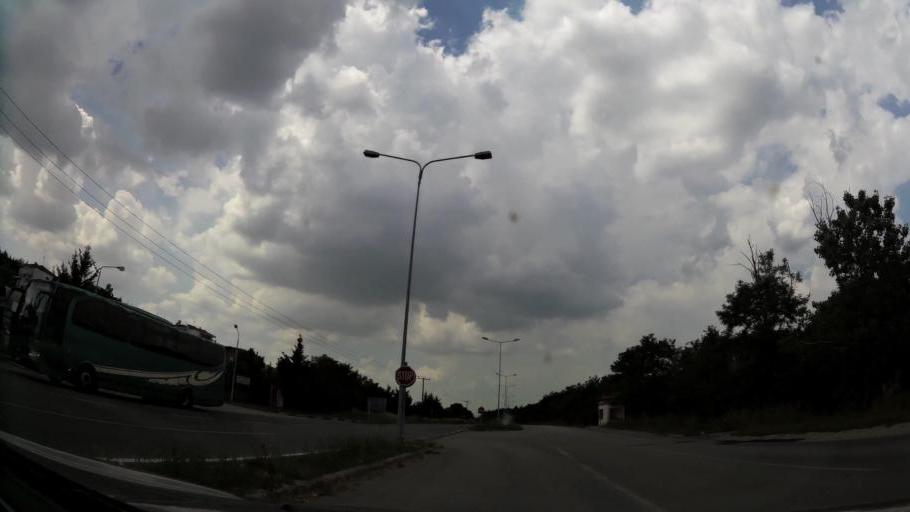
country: GR
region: West Macedonia
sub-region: Nomos Kozanis
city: Koila
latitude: 40.3281
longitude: 21.8274
